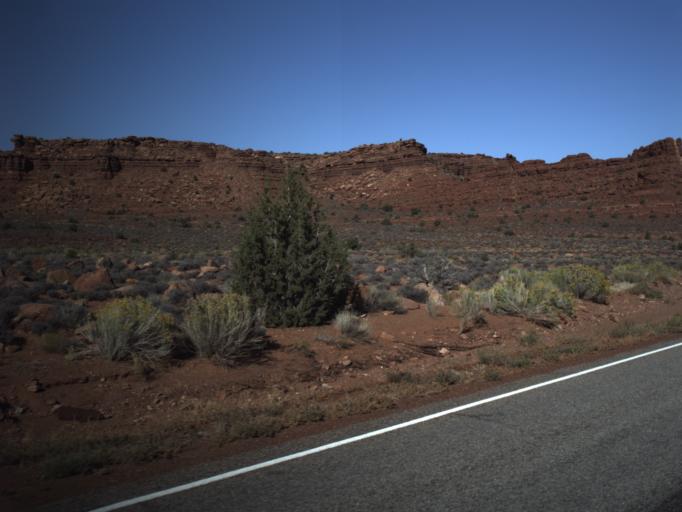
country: US
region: Utah
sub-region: San Juan County
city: Blanding
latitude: 37.7960
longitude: -110.3032
